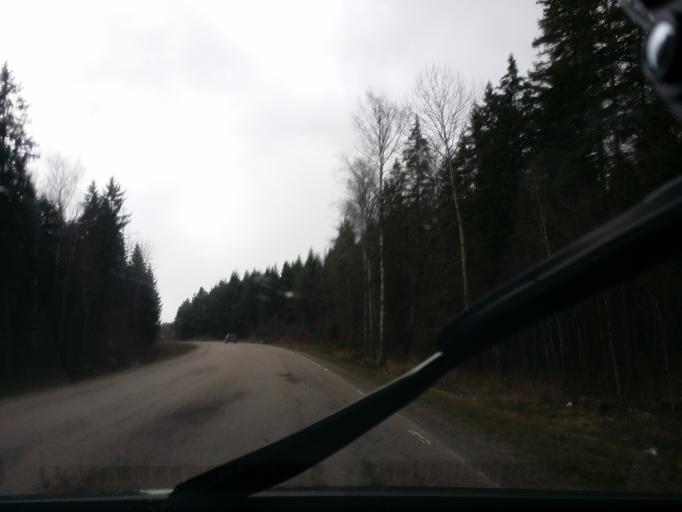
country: SE
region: Uppsala
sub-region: Enkopings Kommun
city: Enkoping
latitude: 59.6342
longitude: 17.1443
